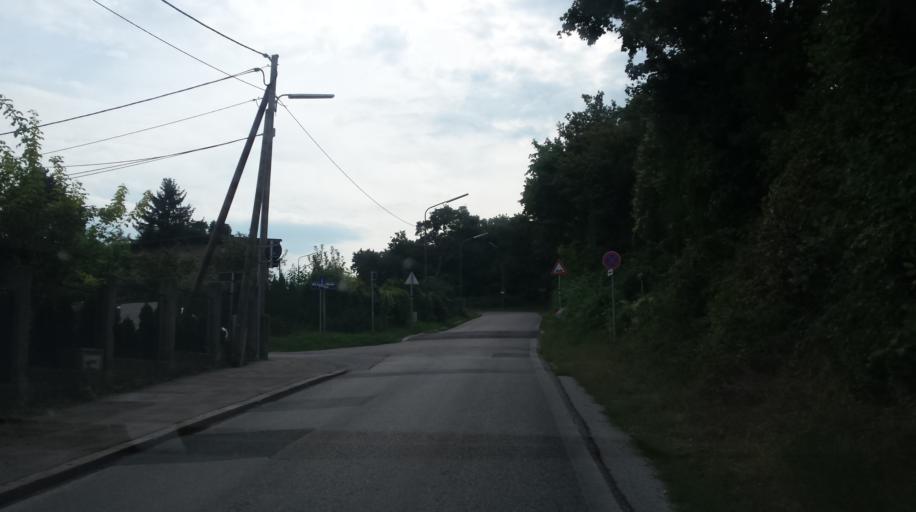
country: AT
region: Vienna
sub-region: Wien Stadt
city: Vienna
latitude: 48.1680
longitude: 16.4031
